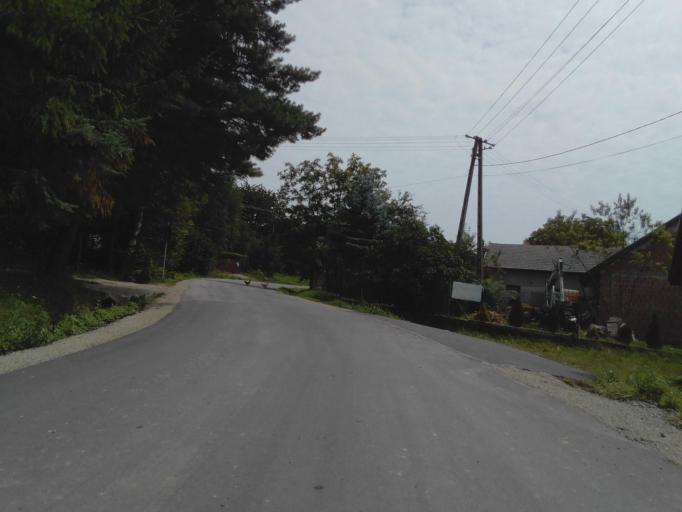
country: PL
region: Subcarpathian Voivodeship
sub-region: Powiat jasielski
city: Tarnowiec
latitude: 49.7712
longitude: 21.5714
